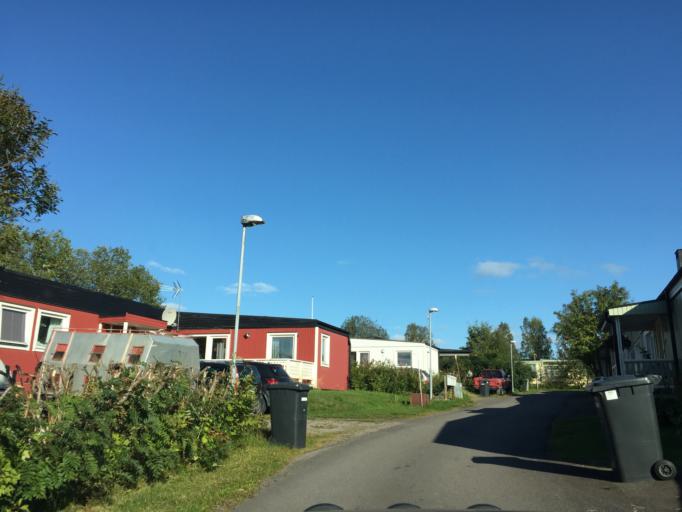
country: SE
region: Norrbotten
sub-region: Gallivare Kommun
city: Malmberget
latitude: 67.6490
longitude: 21.0511
